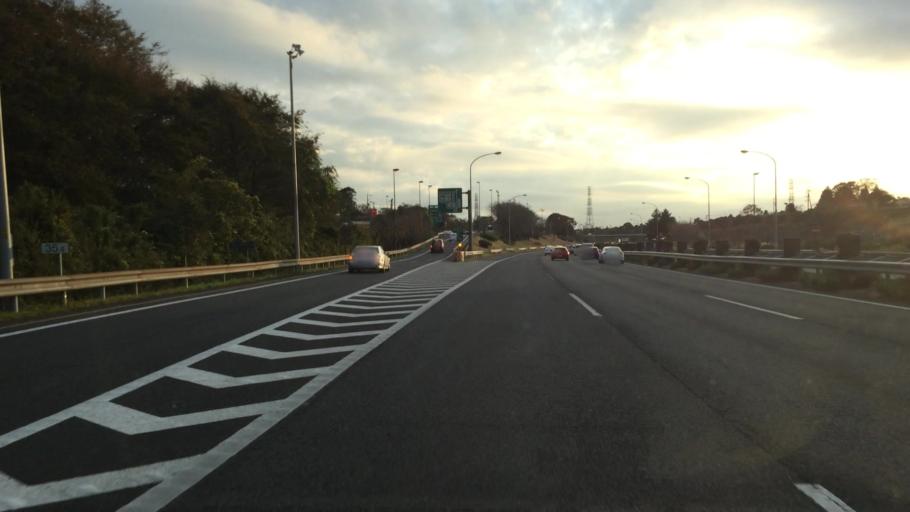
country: JP
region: Chiba
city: Shisui
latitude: 35.7135
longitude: 140.2868
